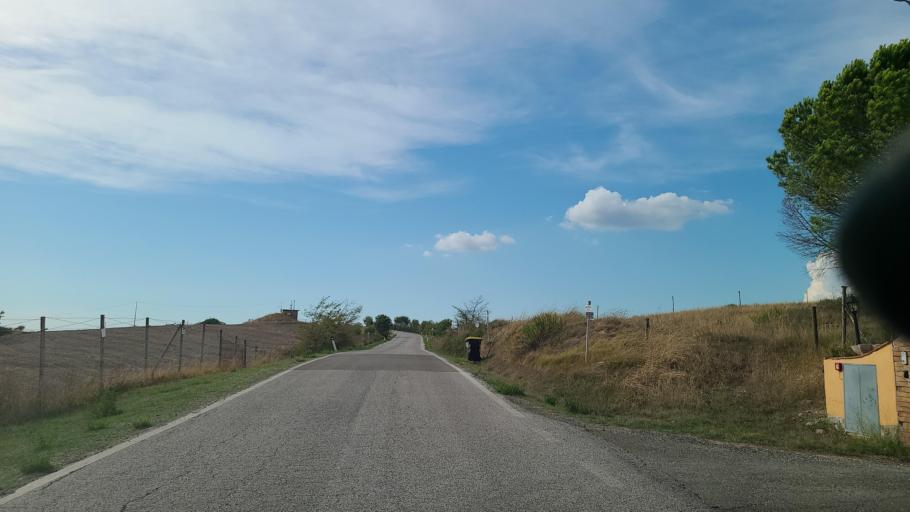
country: IT
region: Tuscany
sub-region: Provincia di Siena
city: San Gimignano
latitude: 43.4402
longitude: 10.9580
